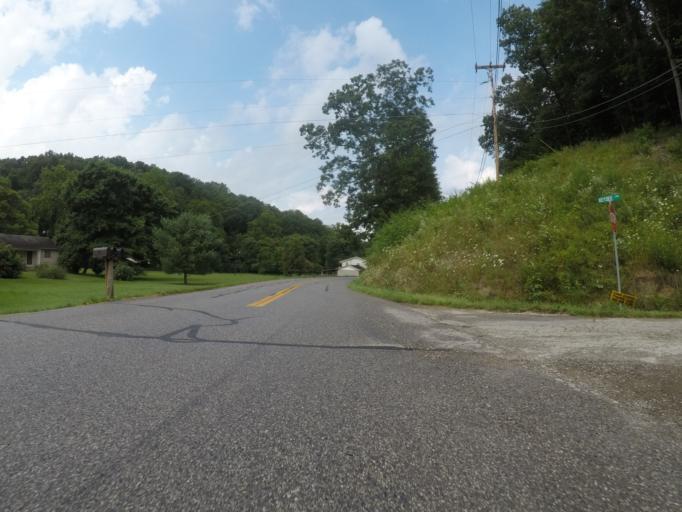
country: US
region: Kentucky
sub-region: Boyd County
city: Meads
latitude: 38.4126
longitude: -82.6762
